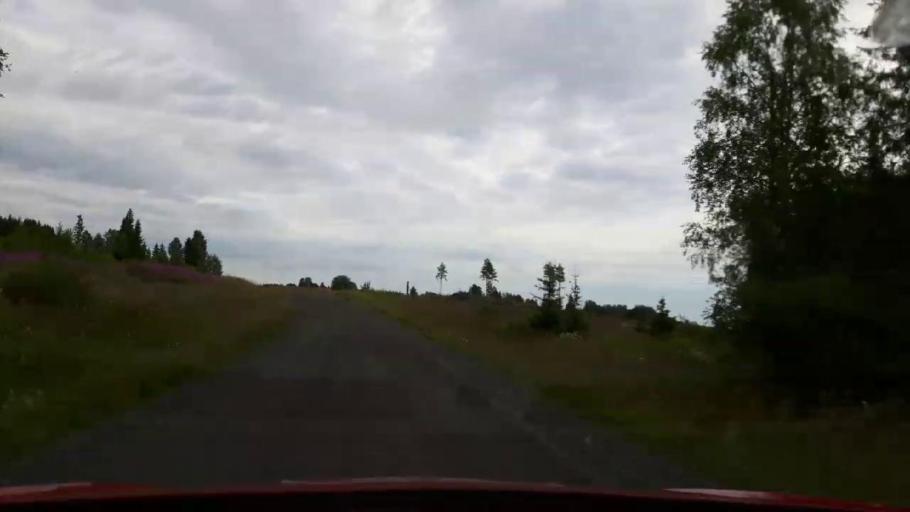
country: SE
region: Jaemtland
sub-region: OEstersunds Kommun
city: Lit
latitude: 63.4104
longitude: 15.2420
